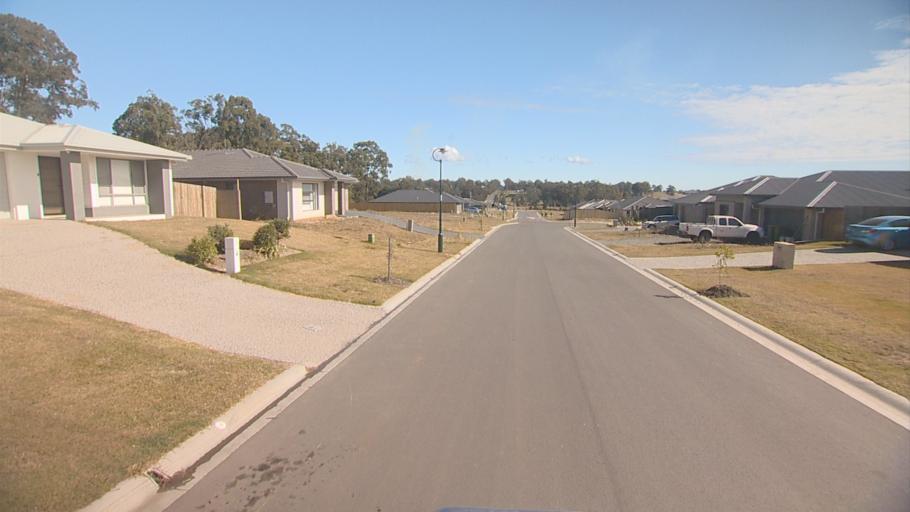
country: AU
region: Queensland
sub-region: Logan
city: Chambers Flat
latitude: -27.7780
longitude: 153.0993
